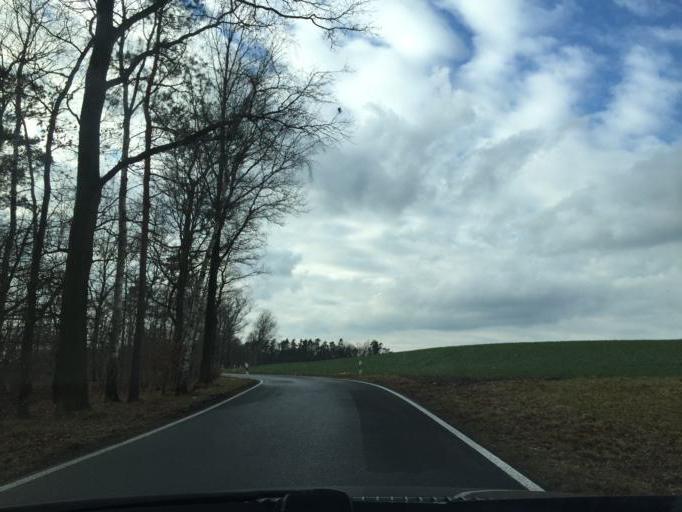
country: DE
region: Saxony
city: Ottendorf-Okrilla
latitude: 51.1693
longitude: 13.8518
